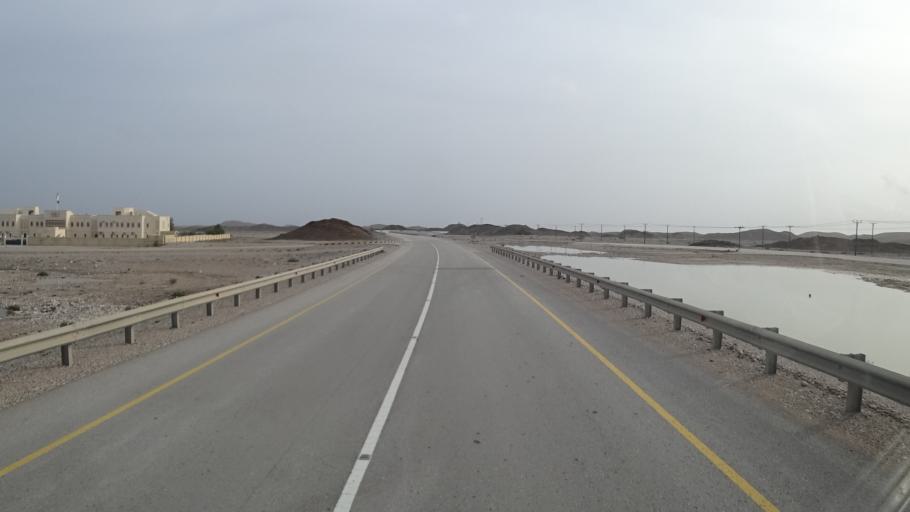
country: OM
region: Zufar
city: Salalah
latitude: 17.0448
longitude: 54.8455
